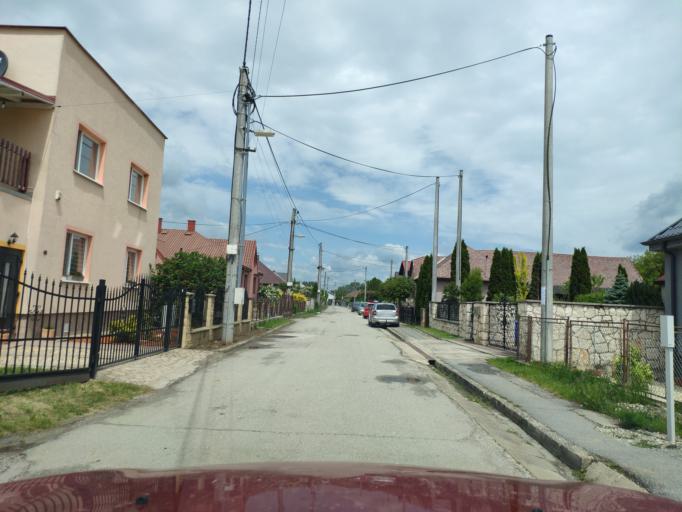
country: SK
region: Kosicky
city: Kosice
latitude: 48.7294
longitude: 21.3392
